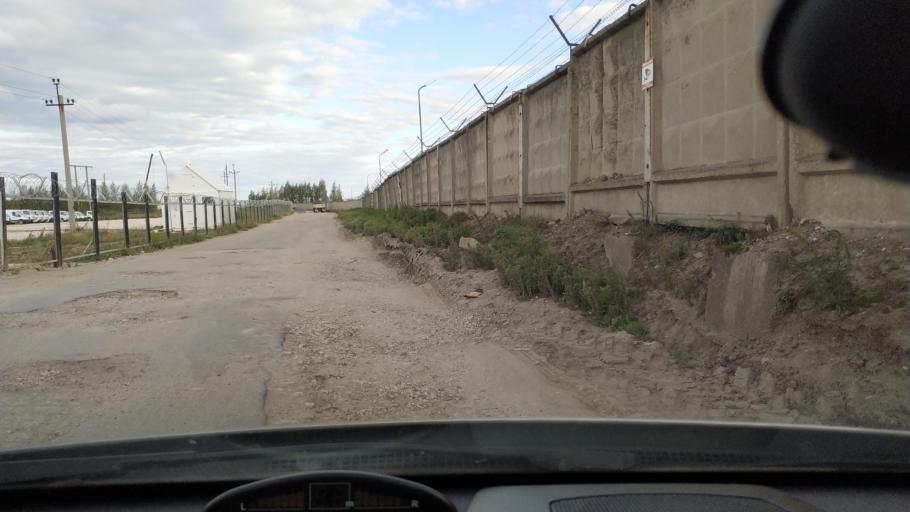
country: RU
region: Rjazan
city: Polyany
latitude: 54.5778
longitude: 39.8410
